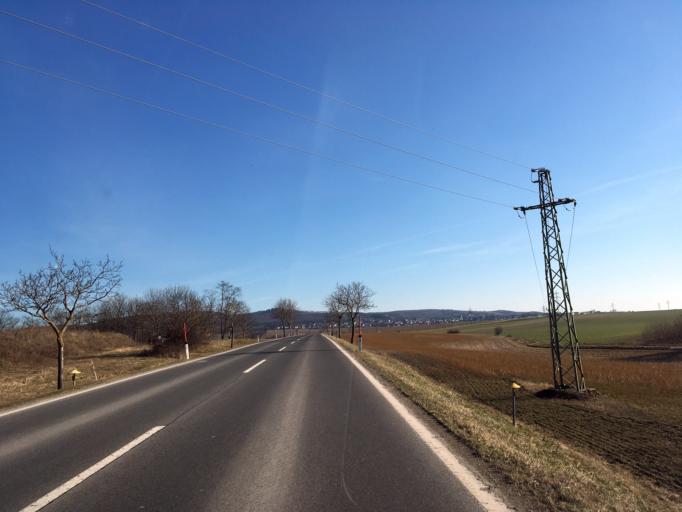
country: AT
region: Burgenland
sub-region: Eisenstadt-Umgebung
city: Wimpassing an der Leitha
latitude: 47.9052
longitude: 16.4348
